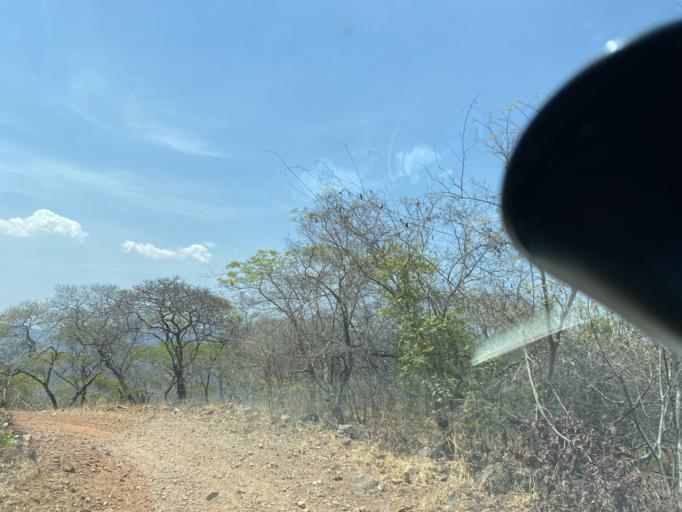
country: ZM
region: Lusaka
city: Kafue
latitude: -15.7989
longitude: 28.4571
